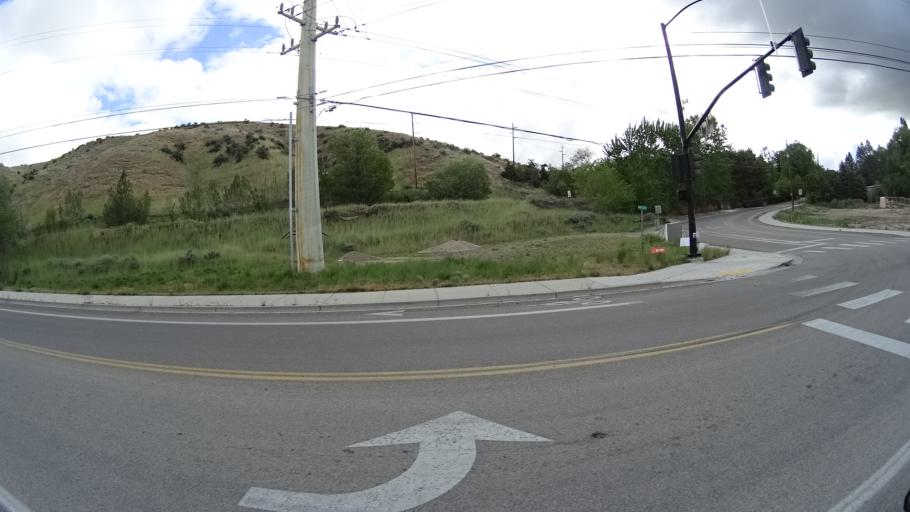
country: US
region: Idaho
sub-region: Ada County
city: Garden City
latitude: 43.6841
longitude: -116.2795
